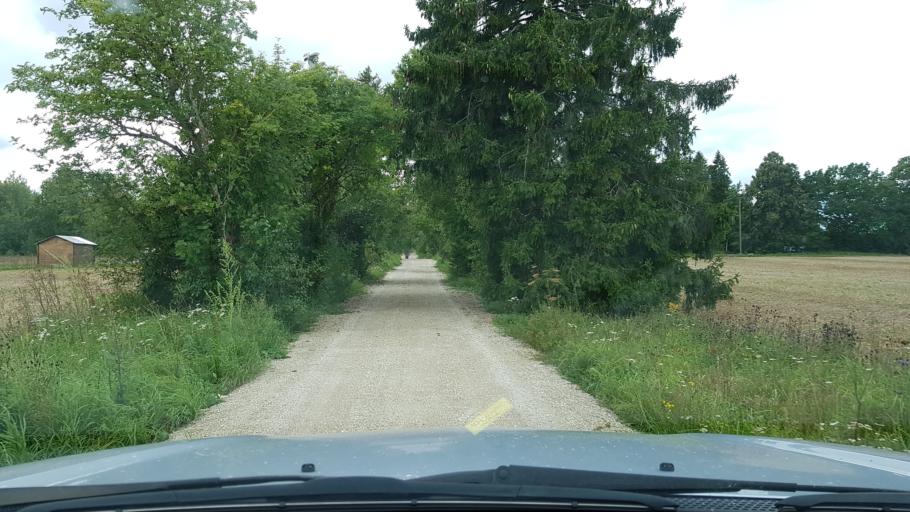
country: EE
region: Harju
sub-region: Rae vald
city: Vaida
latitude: 59.2739
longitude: 25.0249
